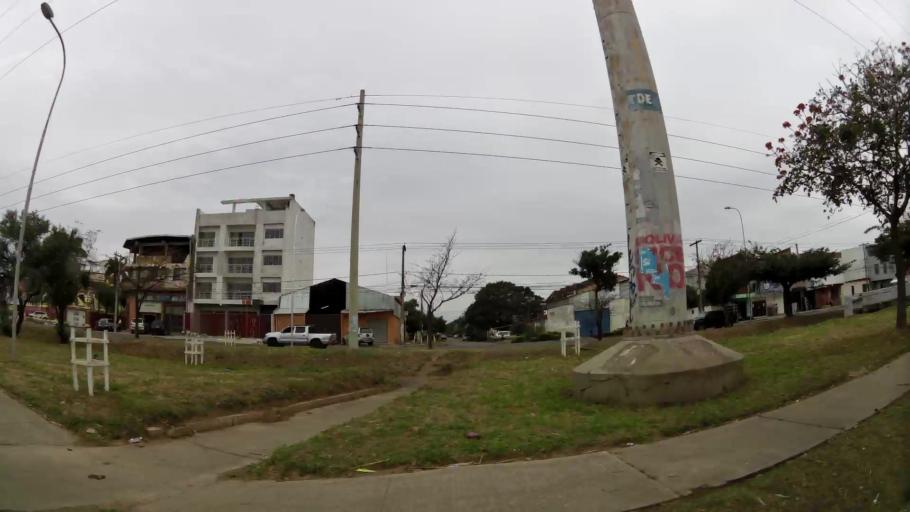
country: BO
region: Santa Cruz
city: Santa Cruz de la Sierra
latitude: -17.7610
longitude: -63.1510
